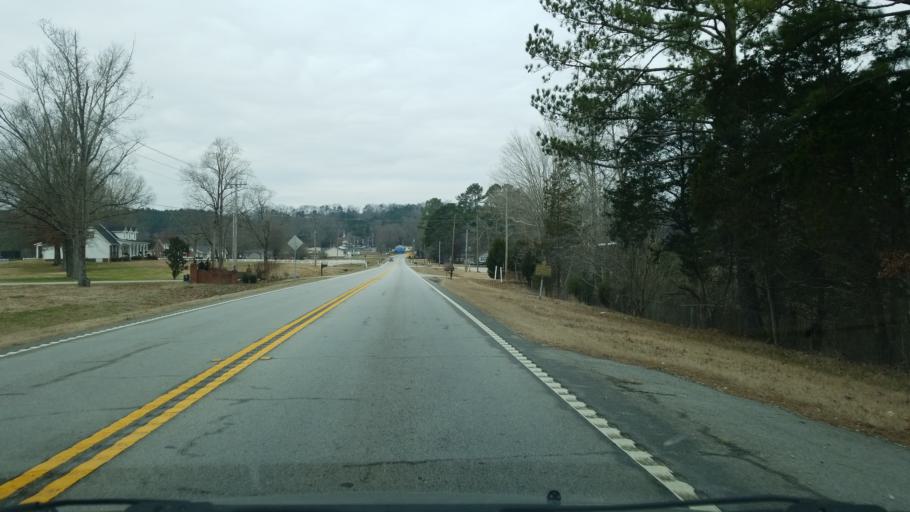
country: US
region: Georgia
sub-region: Catoosa County
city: Indian Springs
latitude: 34.9648
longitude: -85.1772
